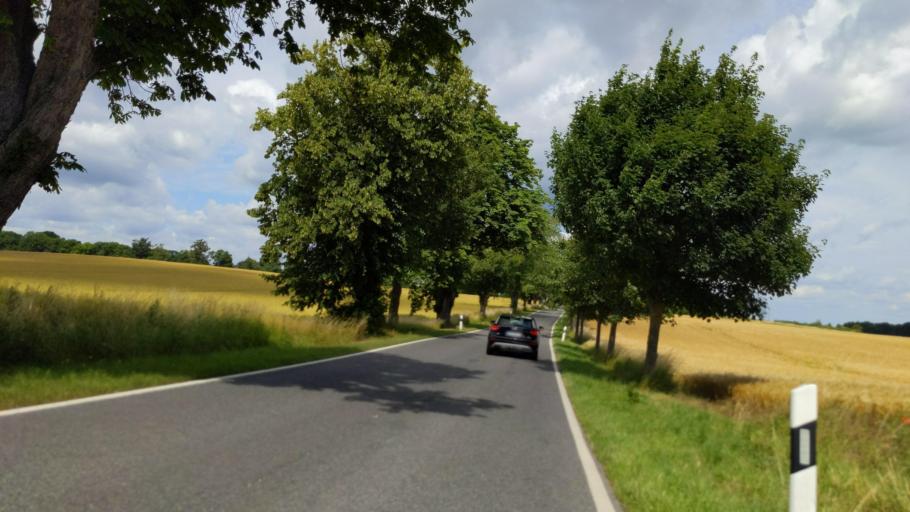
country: DE
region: Mecklenburg-Vorpommern
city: Dassow
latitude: 53.9280
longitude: 10.9730
